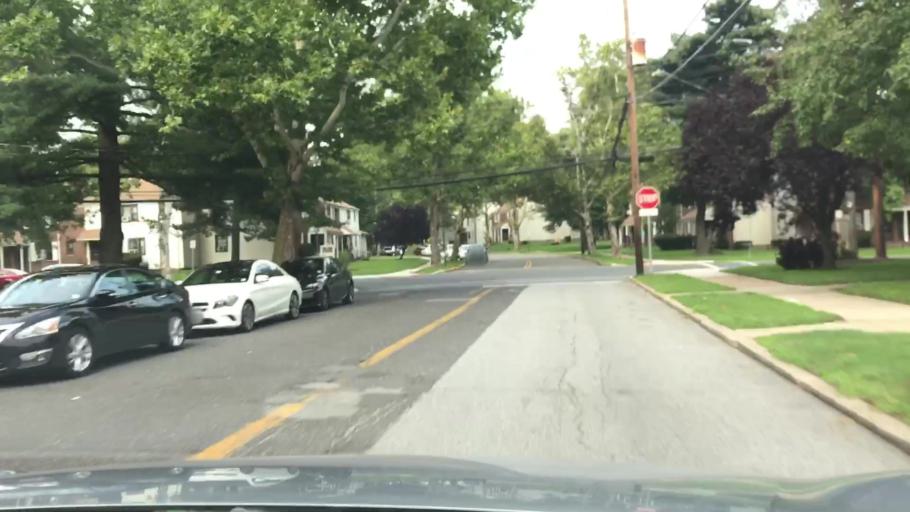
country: US
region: New Jersey
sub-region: Bergen County
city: New Milford
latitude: 40.9255
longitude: -74.0179
